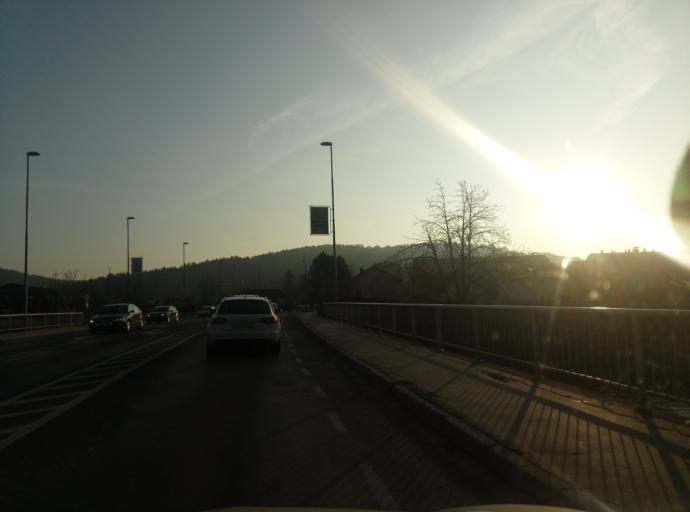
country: SI
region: Ljubljana
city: Ljubljana
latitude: 46.0553
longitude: 14.5404
